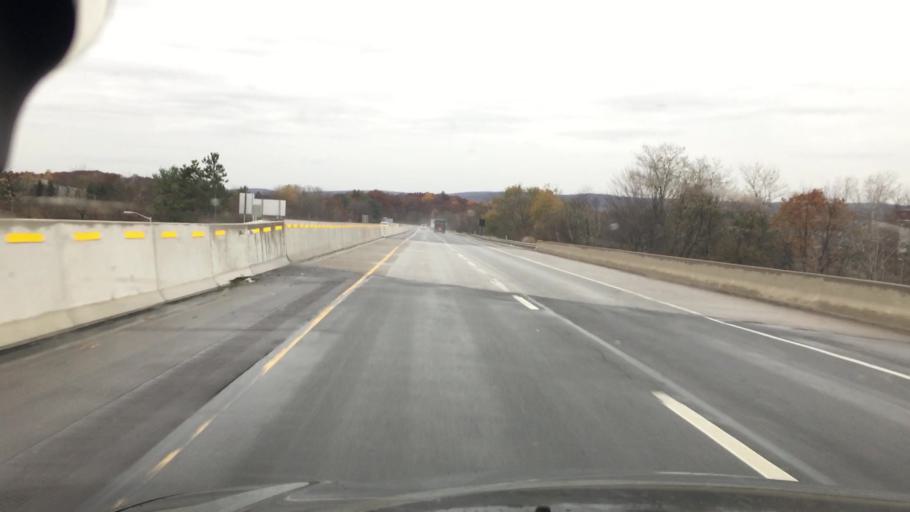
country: US
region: Pennsylvania
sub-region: Luzerne County
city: Ashley
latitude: 41.2005
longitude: -75.9244
